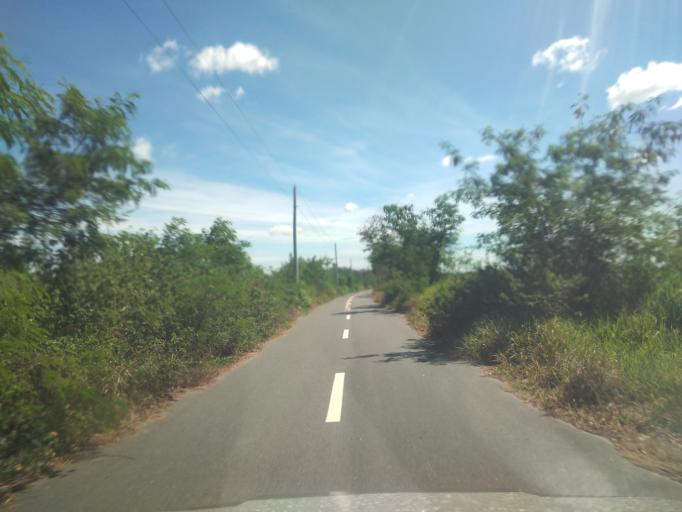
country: PH
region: Central Luzon
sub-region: Province of Pampanga
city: Balas
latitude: 15.0513
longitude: 120.5835
